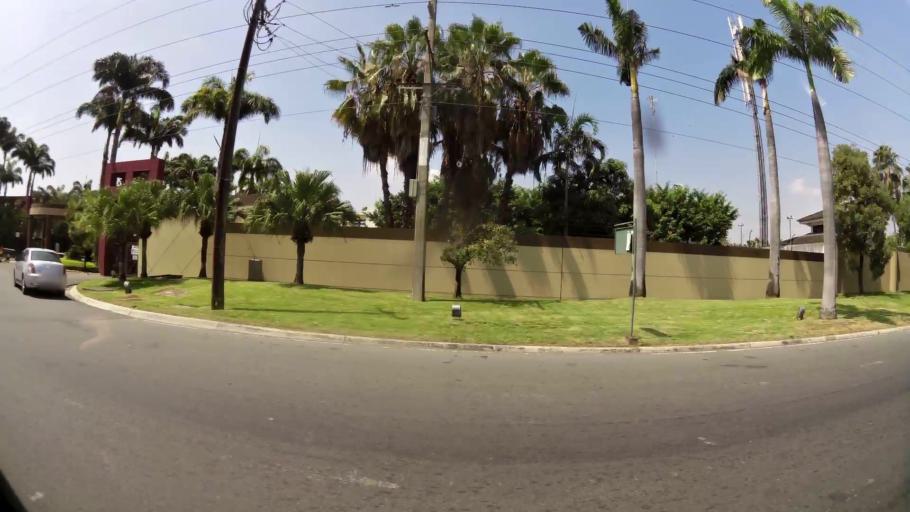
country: EC
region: Guayas
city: Eloy Alfaro
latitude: -2.0932
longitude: -79.8736
